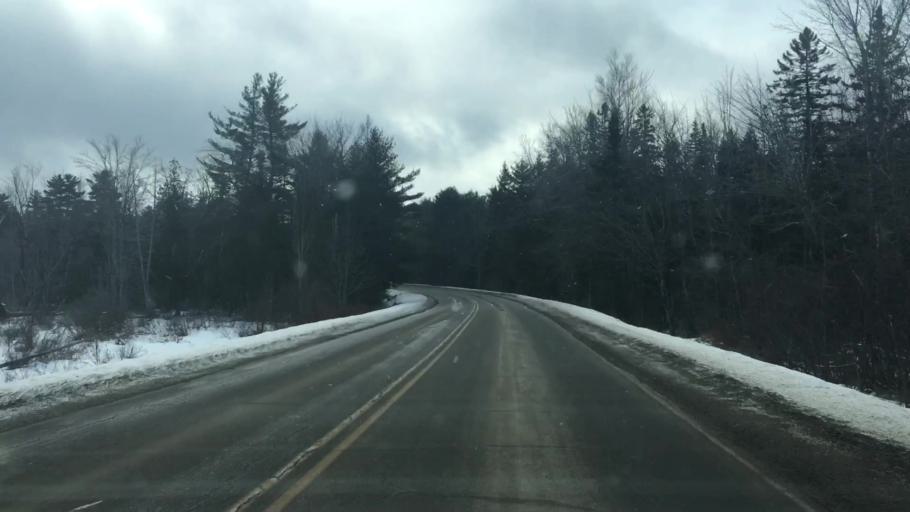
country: US
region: Maine
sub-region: Washington County
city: Calais
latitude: 45.0469
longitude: -67.3274
